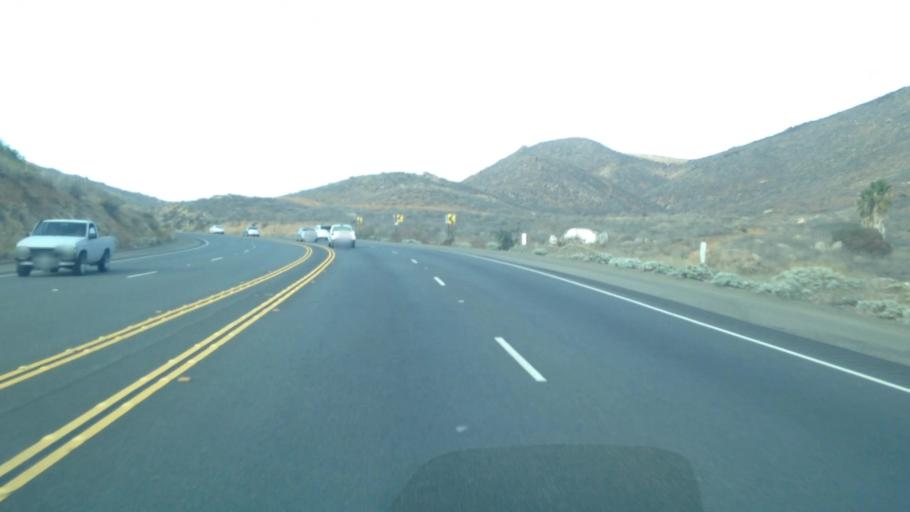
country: US
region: California
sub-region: Riverside County
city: Sunnyslope
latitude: 34.0304
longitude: -117.4302
